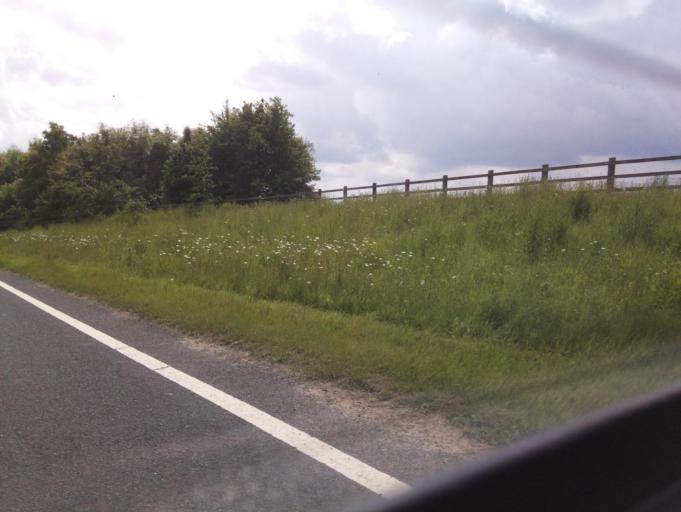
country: GB
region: England
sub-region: North Yorkshire
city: Boroughbridge
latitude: 54.0954
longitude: -1.4079
